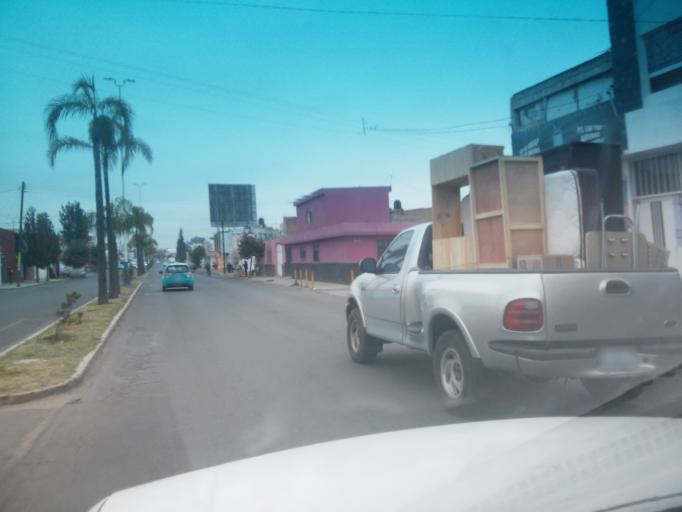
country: MX
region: Durango
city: Victoria de Durango
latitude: 24.0092
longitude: -104.6791
